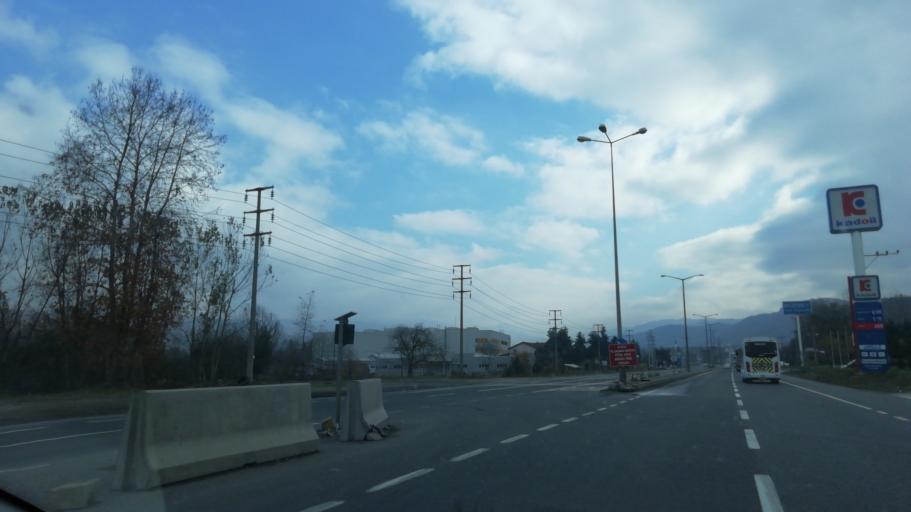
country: TR
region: Duzce
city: Kaynasli
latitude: 40.7814
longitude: 31.2788
